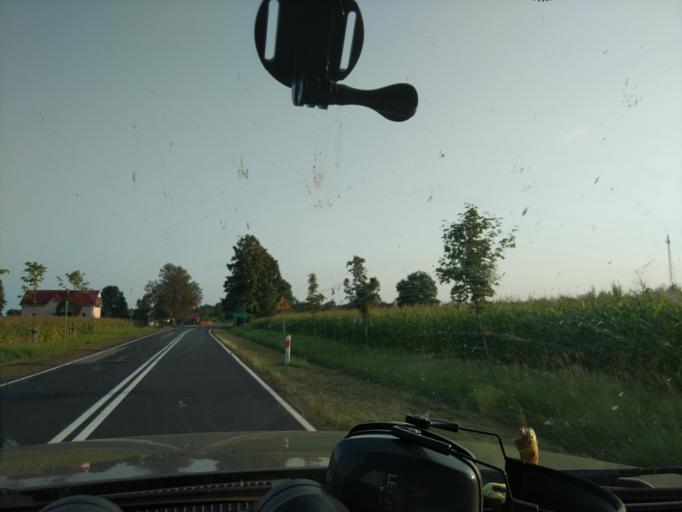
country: PL
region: Warmian-Masurian Voivodeship
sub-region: Powiat szczycienski
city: Wielbark
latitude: 53.3506
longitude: 20.9003
